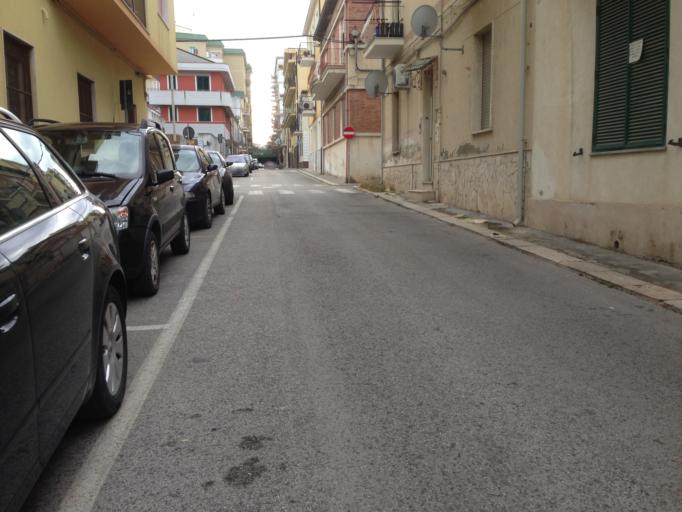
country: IT
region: Molise
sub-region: Provincia di Campobasso
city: Termoli
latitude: 42.0031
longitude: 14.9929
